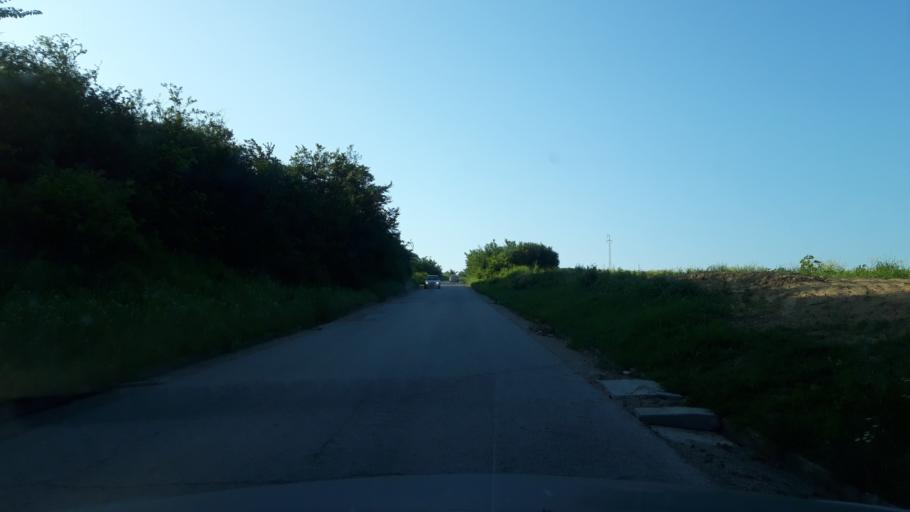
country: RS
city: Celarevo
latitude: 45.1262
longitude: 19.5080
